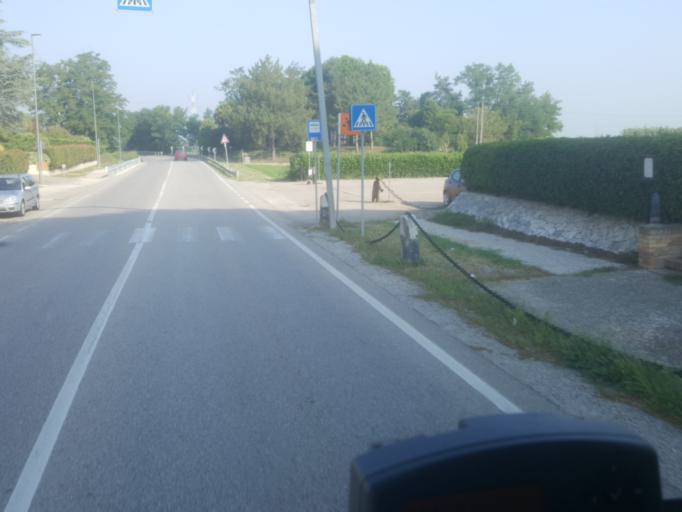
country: IT
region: Emilia-Romagna
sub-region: Provincia di Ravenna
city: Fornace Zarattini
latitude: 44.4439
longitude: 12.1337
